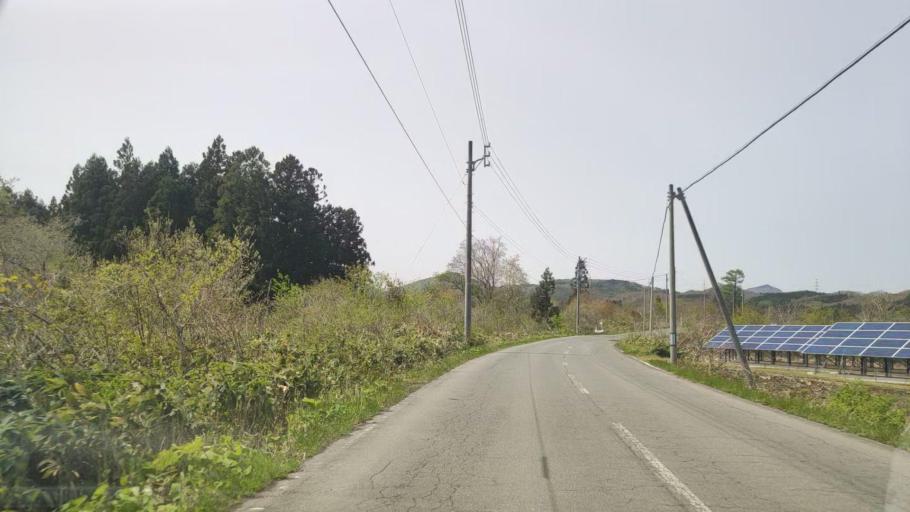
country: JP
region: Aomori
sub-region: Misawa Shi
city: Inuotose
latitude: 40.7844
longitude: 141.1143
